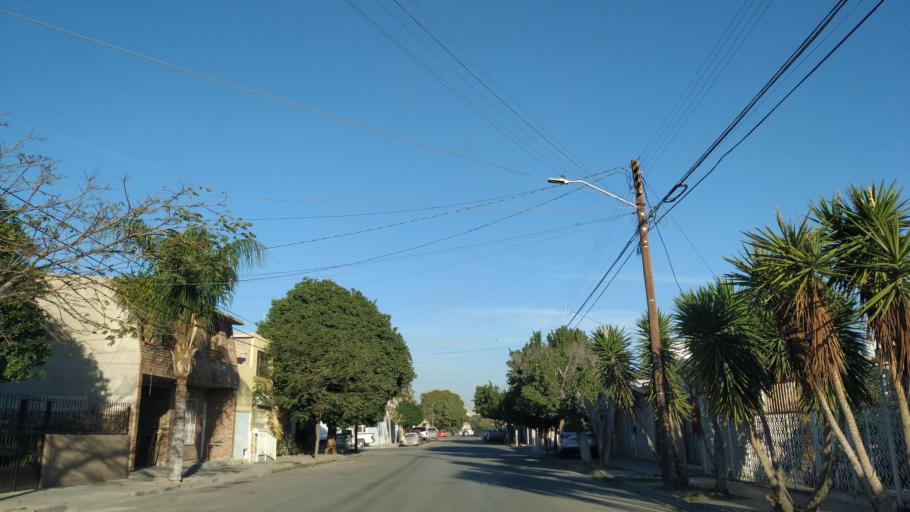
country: MX
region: Coahuila
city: Torreon
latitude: 25.5487
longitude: -103.4552
